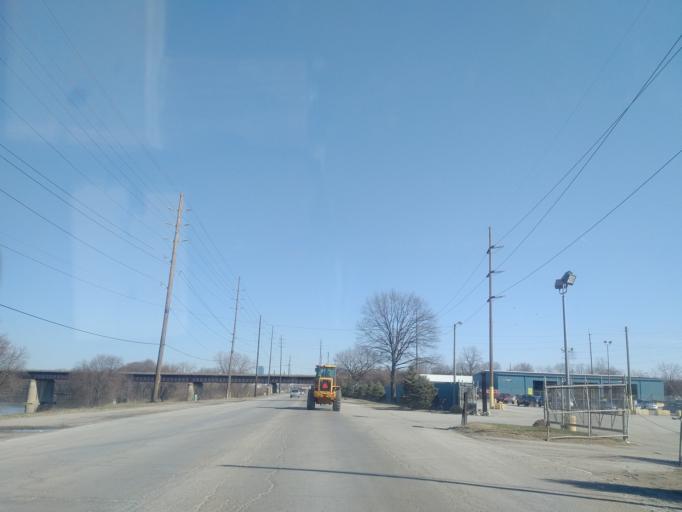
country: US
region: Indiana
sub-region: Marion County
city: Indianapolis
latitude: 39.7388
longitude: -86.1680
